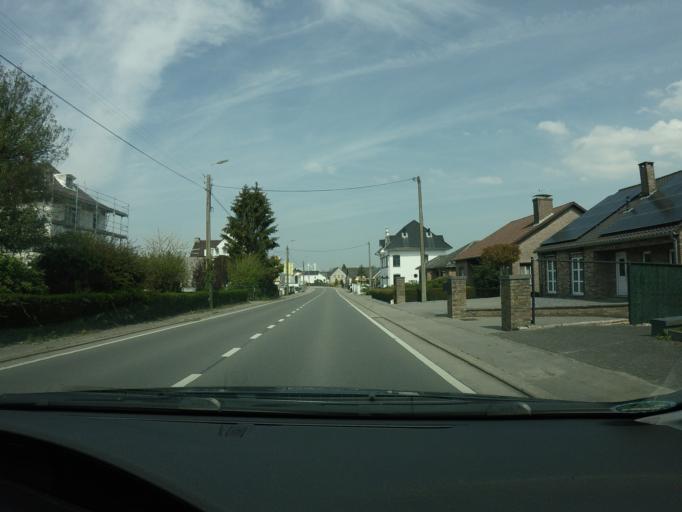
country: NL
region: Limburg
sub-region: Gemeente Maastricht
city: Maastricht
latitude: 50.8063
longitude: 5.6729
